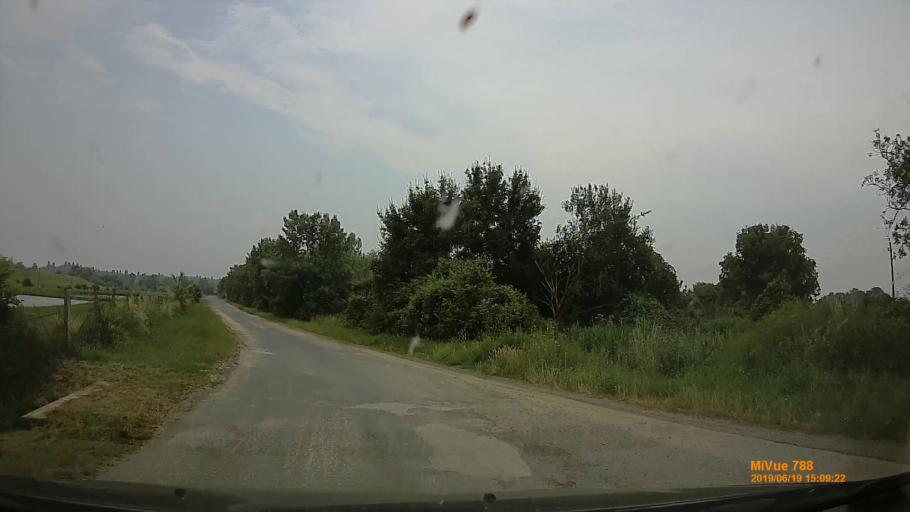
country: HU
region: Baranya
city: Szigetvar
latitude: 46.0845
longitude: 17.8021
